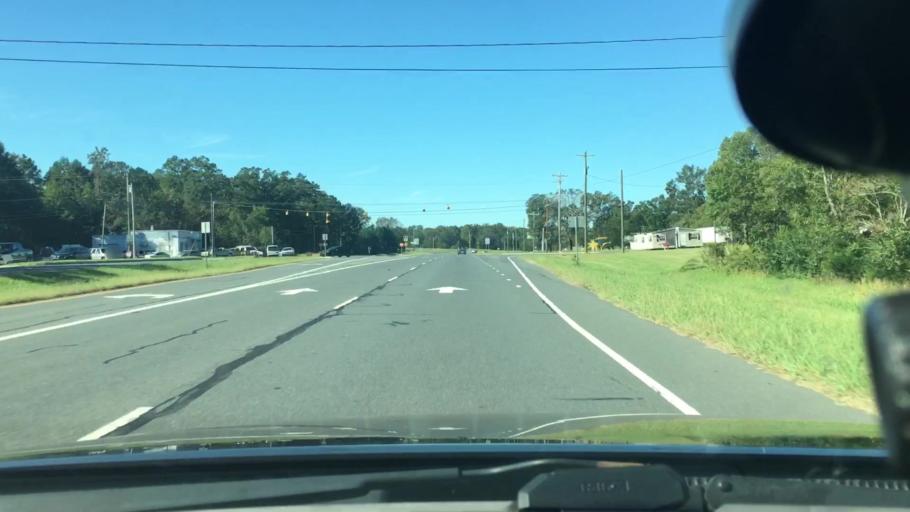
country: US
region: North Carolina
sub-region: Stanly County
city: Oakboro
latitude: 35.2739
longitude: -80.3146
